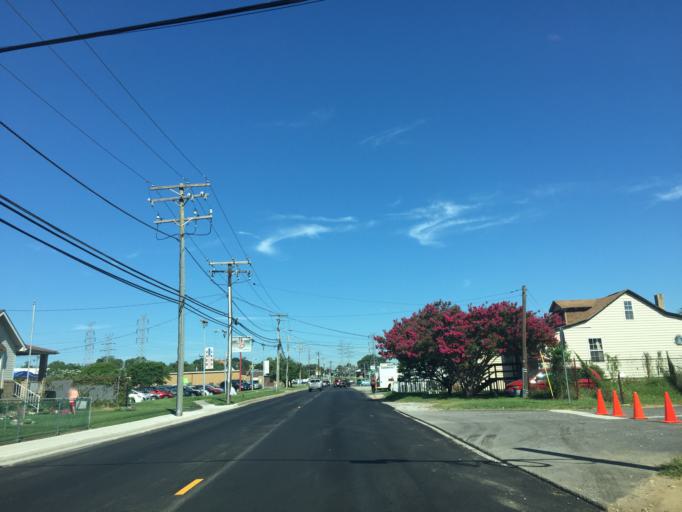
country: US
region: Maryland
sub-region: Baltimore County
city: Essex
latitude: 39.2859
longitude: -76.5020
